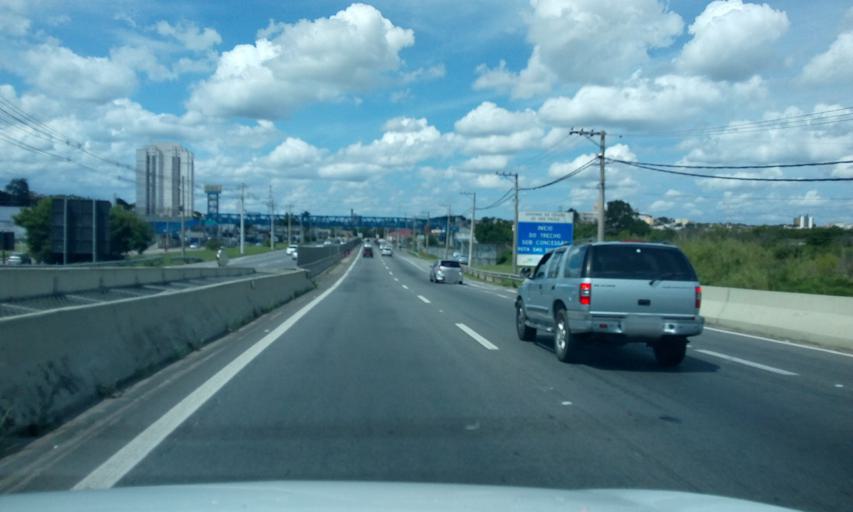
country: BR
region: Sao Paulo
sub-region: Jundiai
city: Jundiai
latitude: -23.1697
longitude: -46.9209
